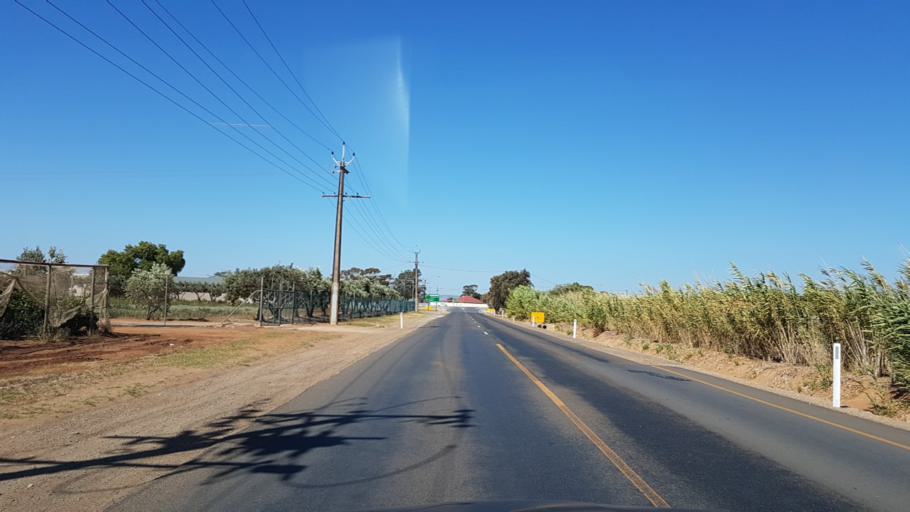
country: AU
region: South Australia
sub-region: Playford
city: Virginia
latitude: -34.7255
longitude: 138.5767
